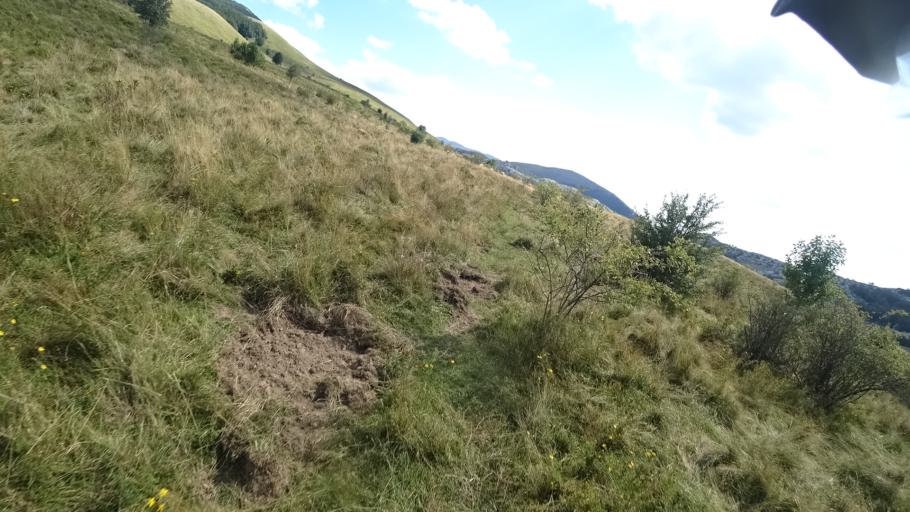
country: HR
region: Zadarska
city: Gracac
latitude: 44.4159
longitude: 16.0018
